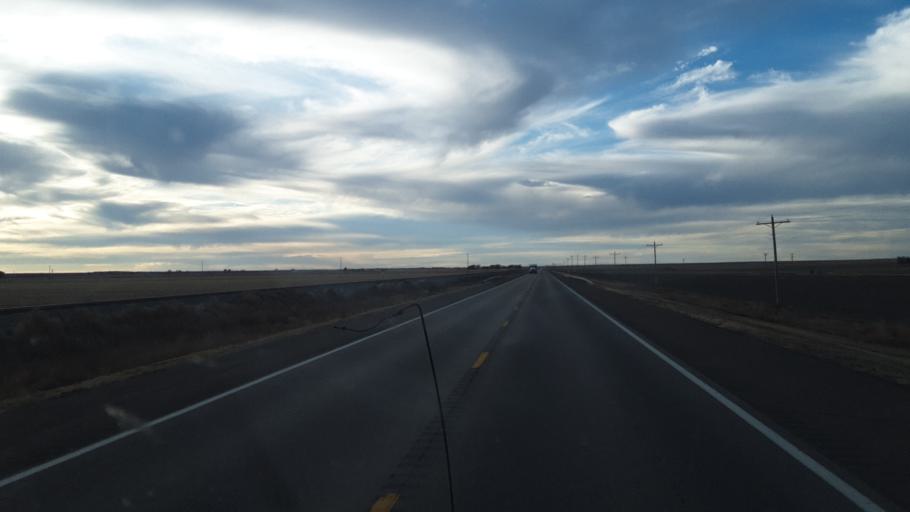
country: US
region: Kansas
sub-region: Hamilton County
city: Syracuse
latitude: 37.9991
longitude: -101.8251
